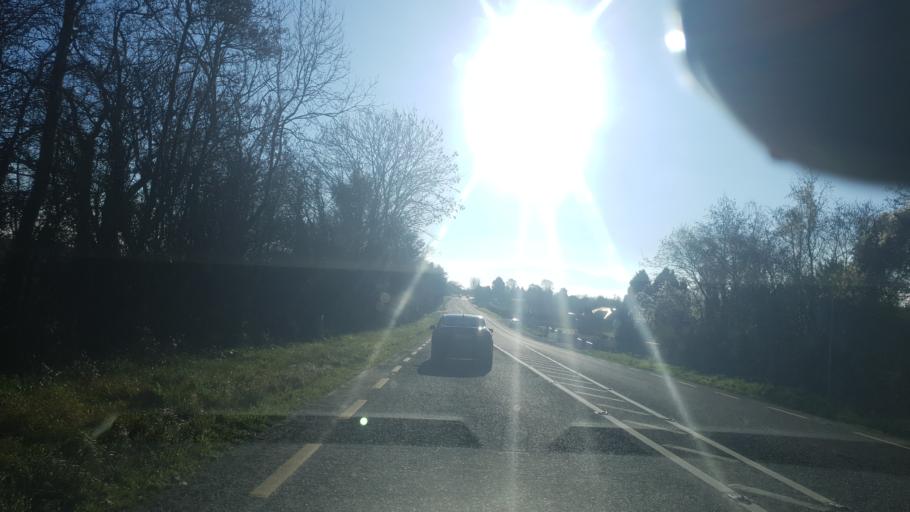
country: IE
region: Munster
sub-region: Ciarrai
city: Cill Airne
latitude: 52.1146
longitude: -9.5170
